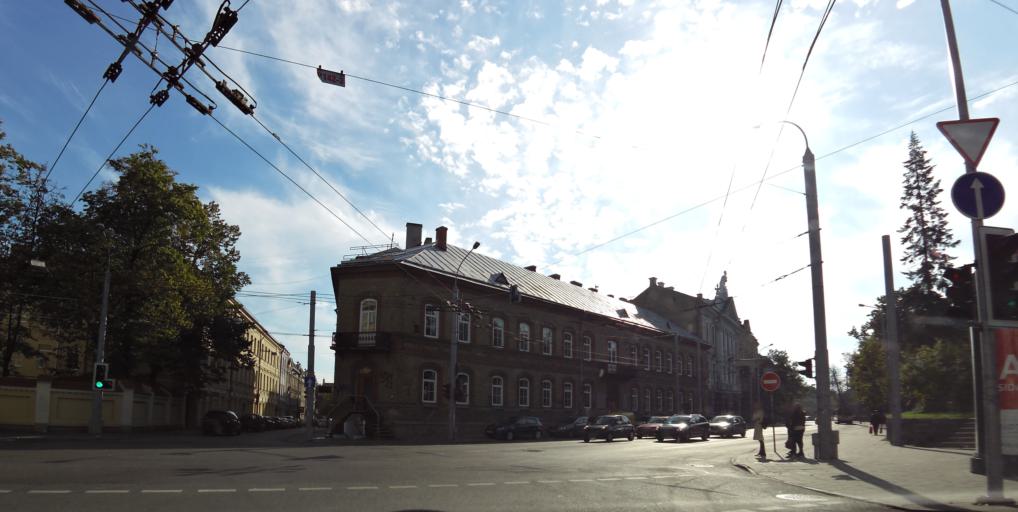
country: LT
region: Vilnius County
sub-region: Vilnius
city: Vilnius
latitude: 54.6846
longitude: 25.2769
